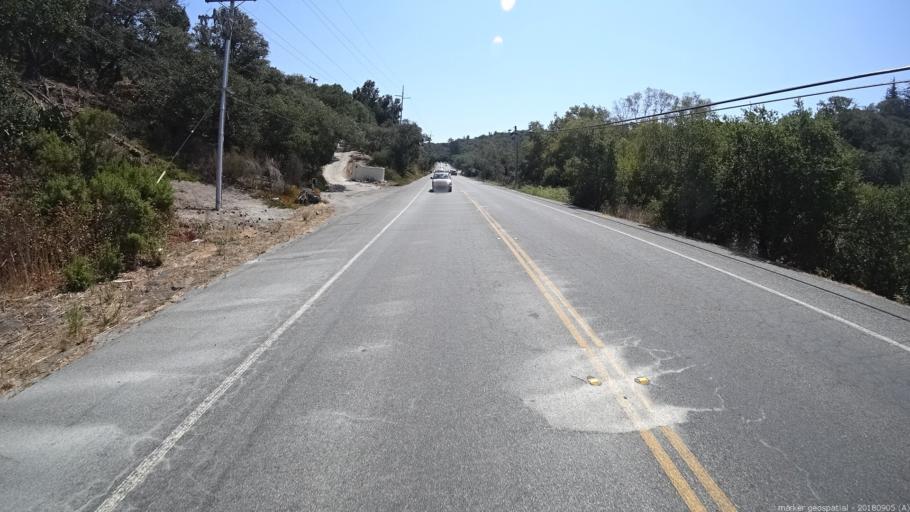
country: US
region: California
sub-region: Monterey County
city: Carmel Valley Village
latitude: 36.5668
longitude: -121.7549
